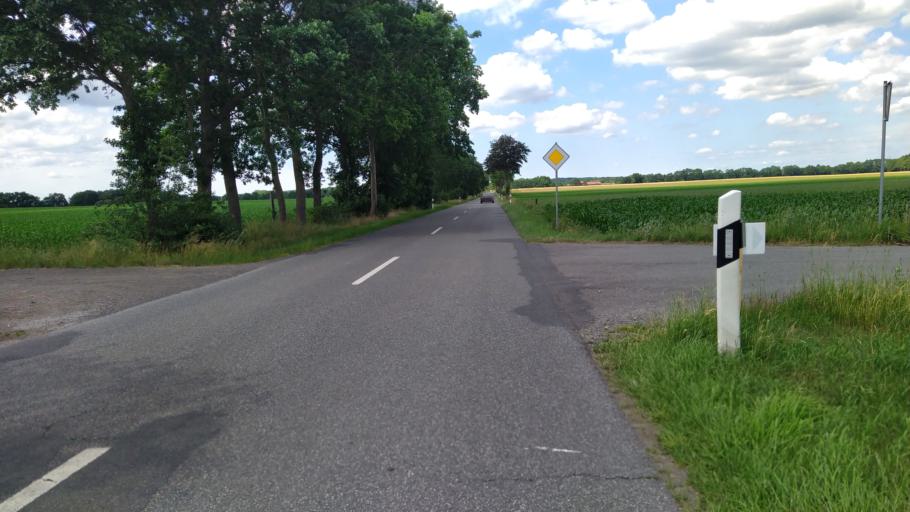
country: DE
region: Lower Saxony
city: Hollnseth
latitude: 53.5763
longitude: 9.1122
